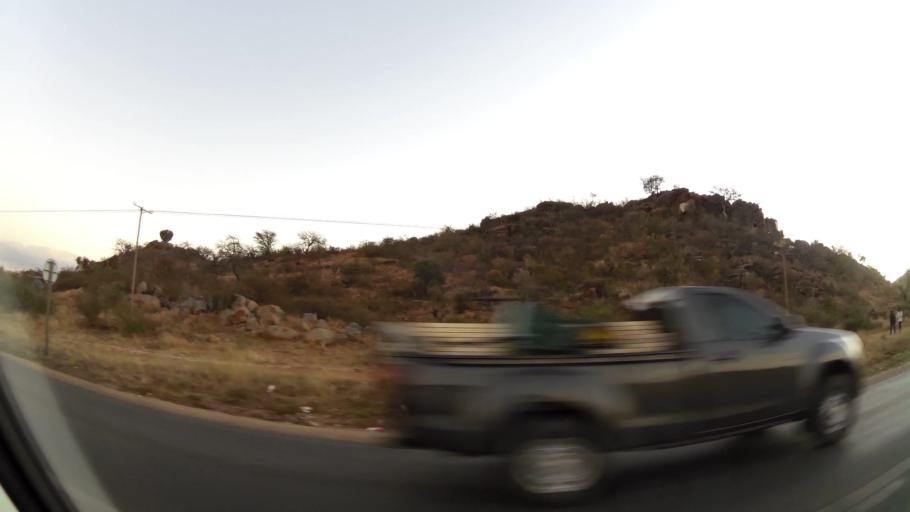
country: ZA
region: Limpopo
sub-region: Waterberg District Municipality
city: Mokopane
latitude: -24.1560
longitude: 28.9786
